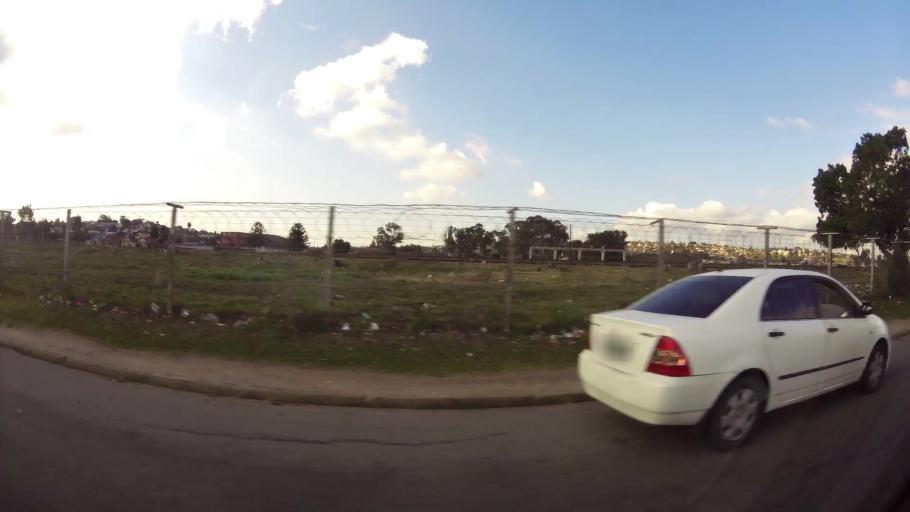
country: ZA
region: Eastern Cape
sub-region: Nelson Mandela Bay Metropolitan Municipality
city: Uitenhage
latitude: -33.7758
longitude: 25.4056
